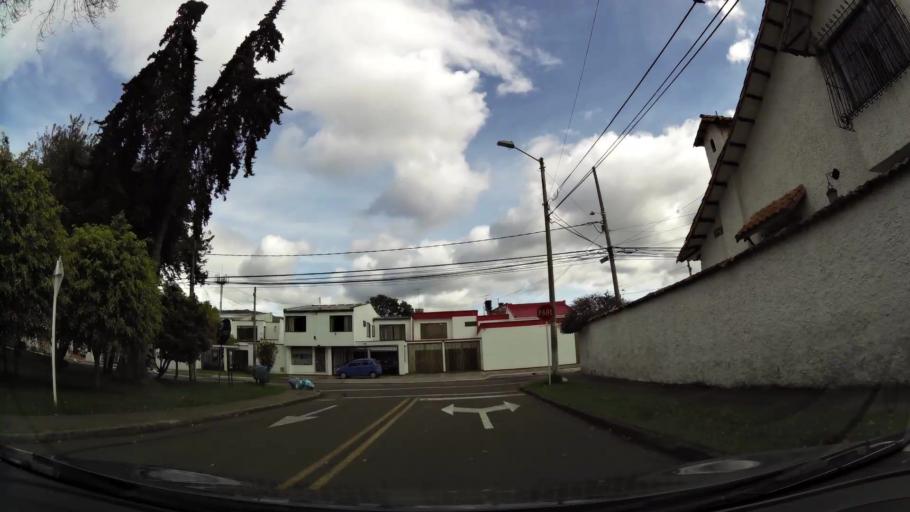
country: CO
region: Bogota D.C.
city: Barrio San Luis
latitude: 4.6926
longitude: -74.0648
